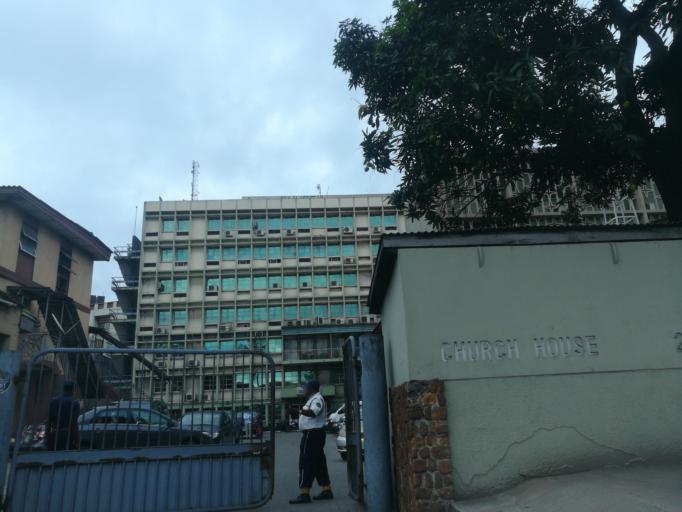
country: NG
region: Lagos
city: Lagos
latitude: 6.4504
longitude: 3.3907
